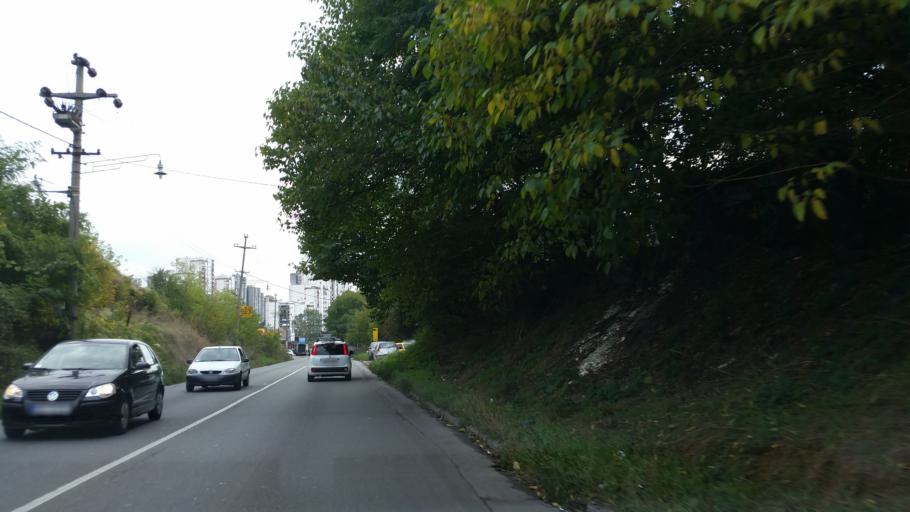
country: RS
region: Central Serbia
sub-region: Belgrade
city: Zemun
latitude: 44.8056
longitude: 20.3644
